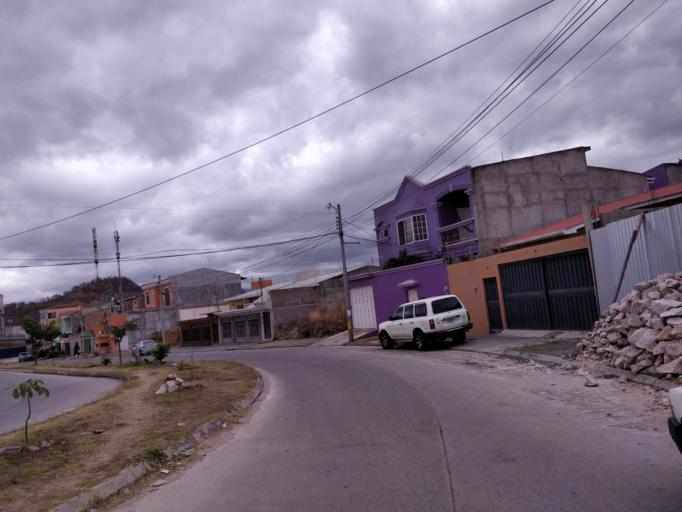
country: HN
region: Francisco Morazan
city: Yaguacire
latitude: 14.0345
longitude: -87.2393
